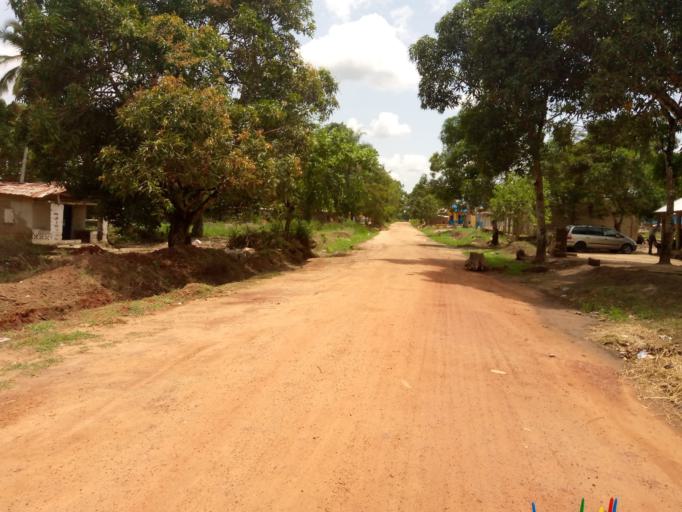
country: SL
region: Western Area
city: Waterloo
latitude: 8.3536
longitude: -12.9599
